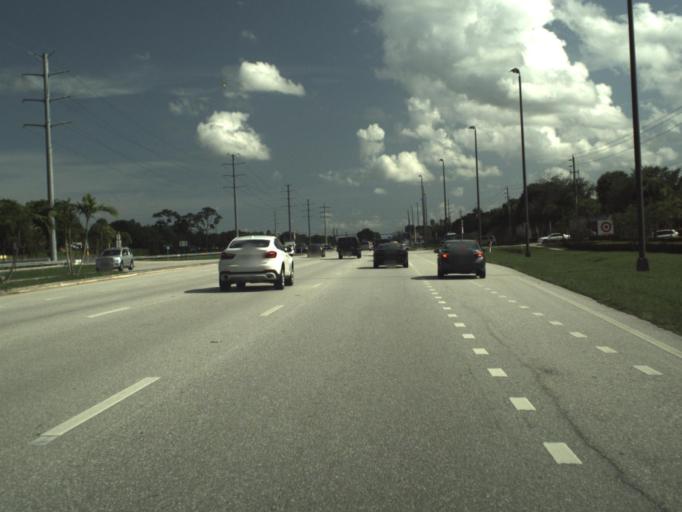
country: US
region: Florida
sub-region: Palm Beach County
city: Boca Pointe
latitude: 26.3557
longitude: -80.2035
